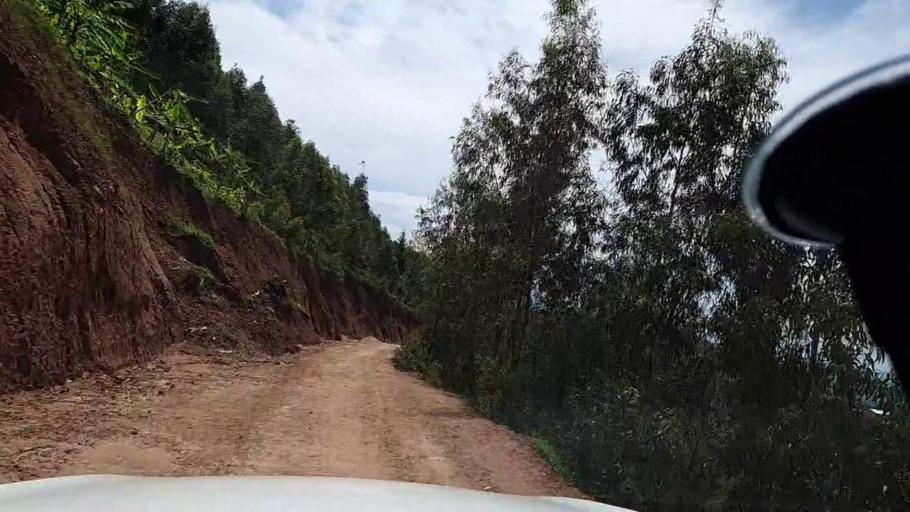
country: RW
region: Southern Province
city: Gitarama
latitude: -2.0810
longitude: 29.6647
